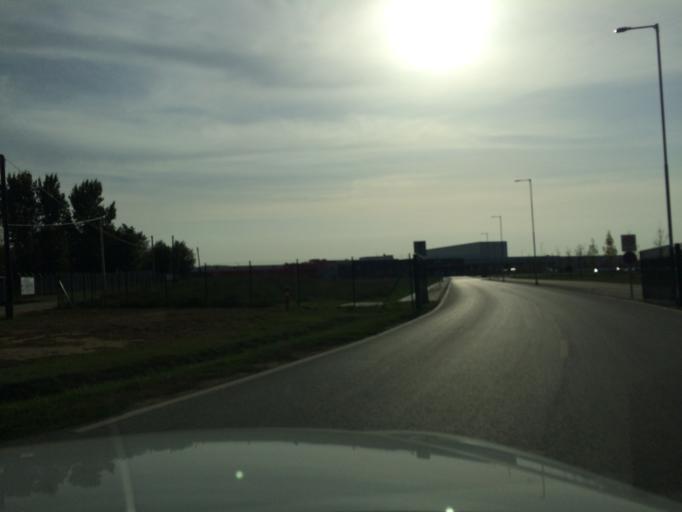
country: HU
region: Szabolcs-Szatmar-Bereg
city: Nyirtelek
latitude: 47.9538
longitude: 21.6504
